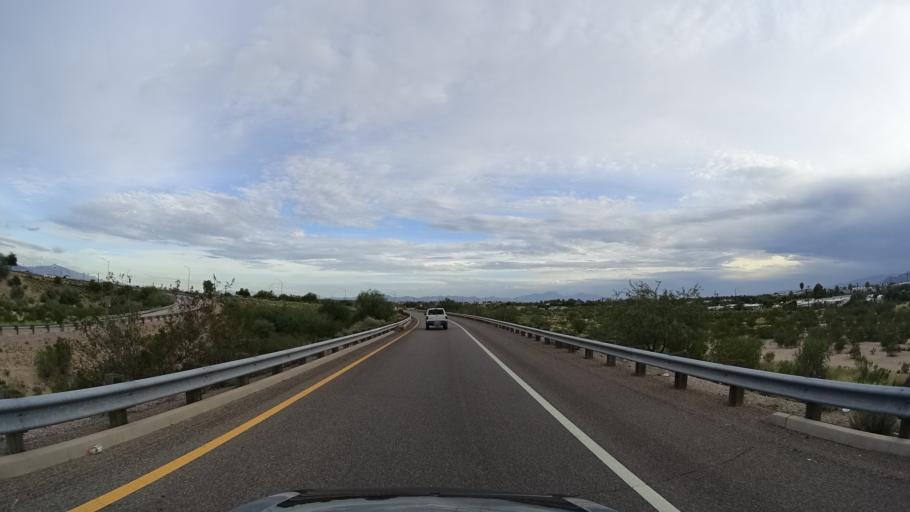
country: US
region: Arizona
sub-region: Pima County
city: South Tucson
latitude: 32.1767
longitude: -110.9463
